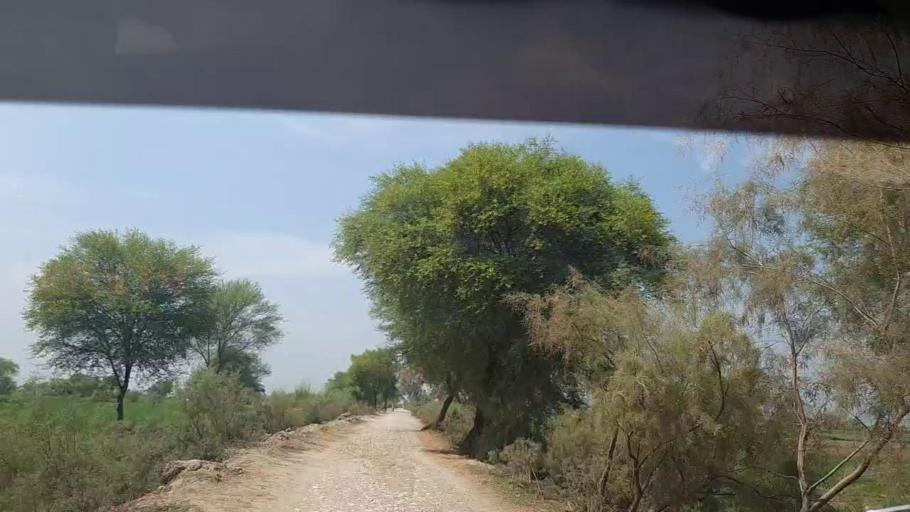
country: PK
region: Sindh
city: Thul
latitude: 28.2064
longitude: 68.6930
